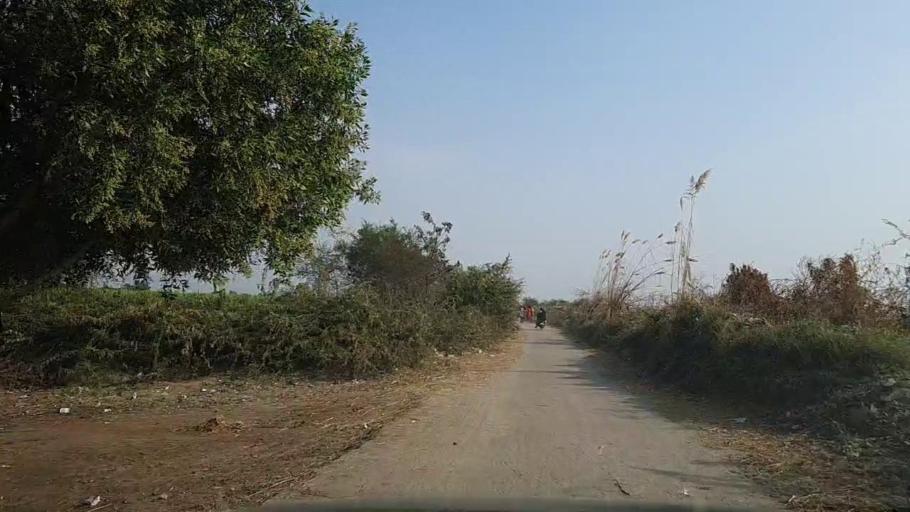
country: PK
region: Sindh
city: Thatta
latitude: 24.6497
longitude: 67.9248
